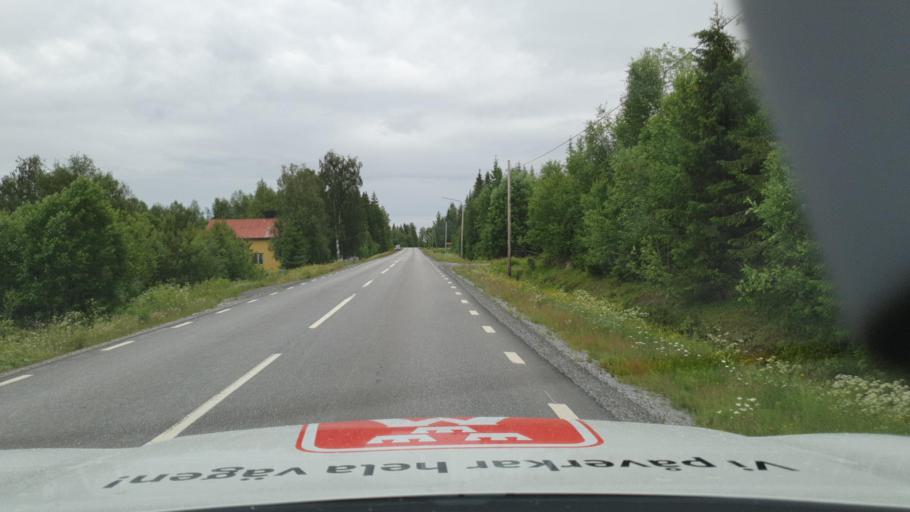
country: SE
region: Vaesterbotten
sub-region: Bjurholms Kommun
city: Bjurholm
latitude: 63.7326
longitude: 19.3238
